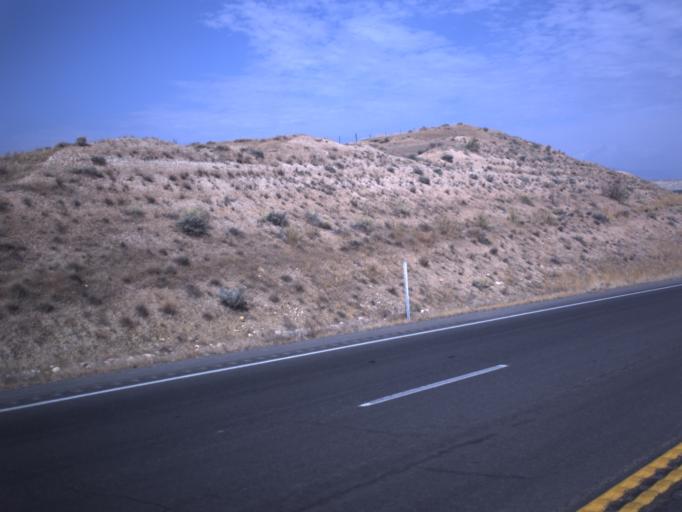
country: US
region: Utah
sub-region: Uintah County
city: Naples
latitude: 40.3669
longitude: -109.3240
